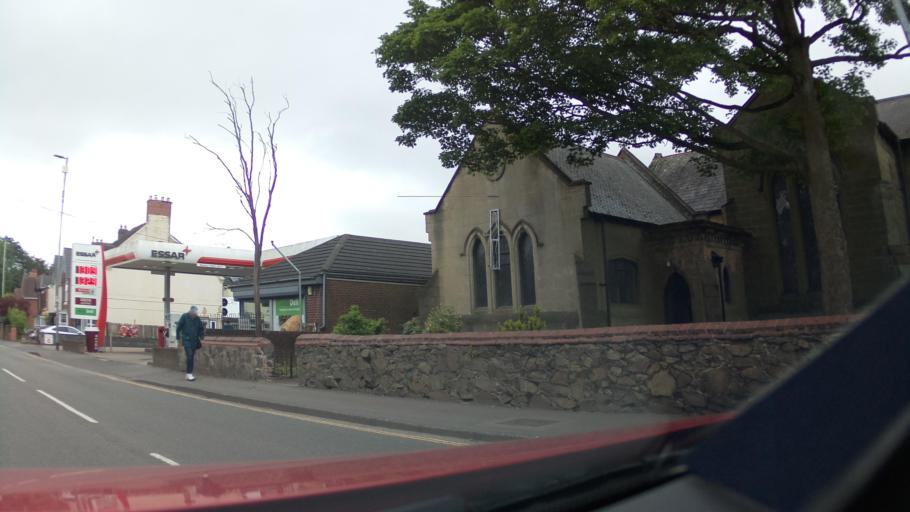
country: GB
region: England
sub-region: Leicestershire
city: Coalville
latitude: 52.7232
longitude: -1.3672
